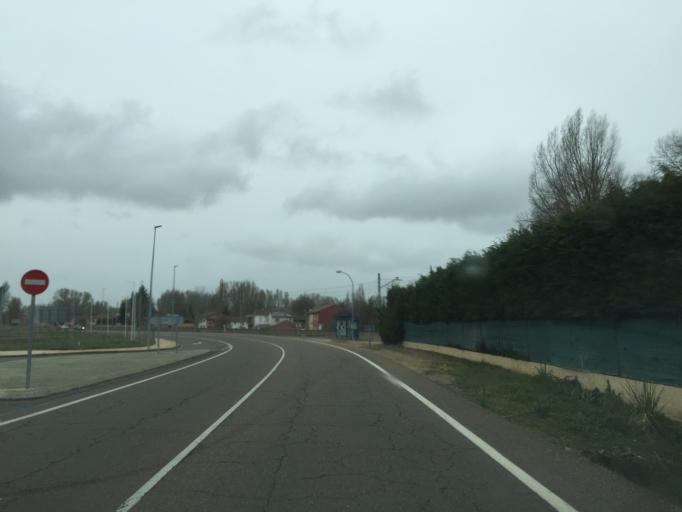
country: ES
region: Castille and Leon
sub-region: Provincia de Leon
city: Sariegos
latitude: 42.6423
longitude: -5.6141
